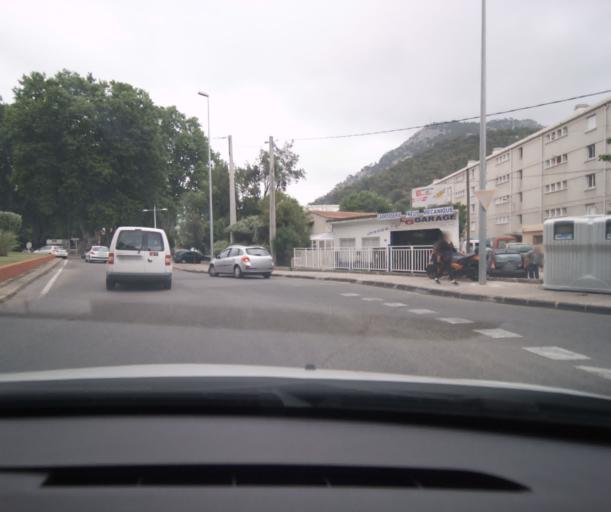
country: FR
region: Provence-Alpes-Cote d'Azur
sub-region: Departement du Var
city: Toulon
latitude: 43.1416
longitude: 5.9106
